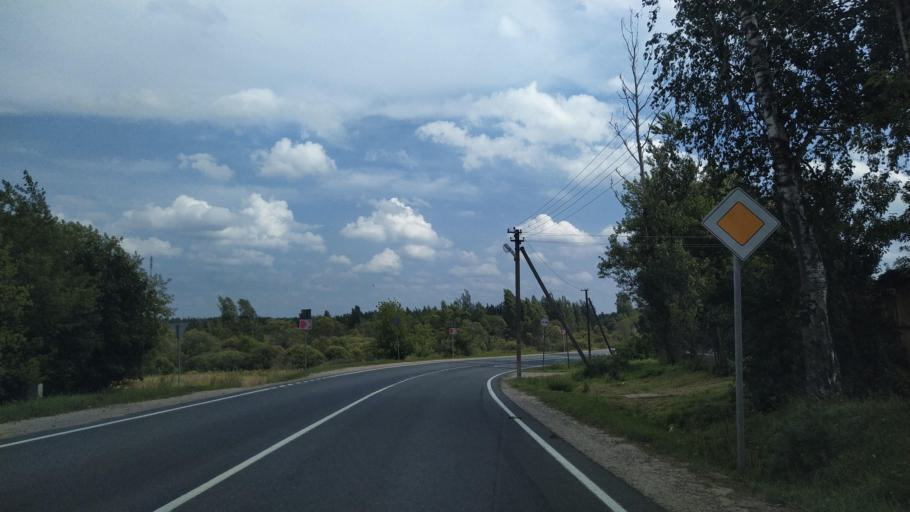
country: RU
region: Pskov
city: Pskov
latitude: 57.7605
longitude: 28.7681
